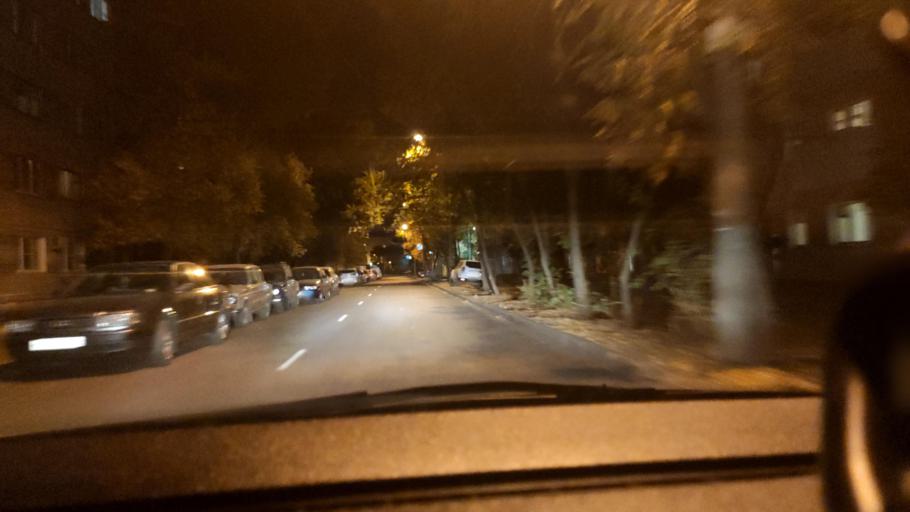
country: RU
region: Voronezj
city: Voronezh
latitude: 51.6394
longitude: 39.2451
